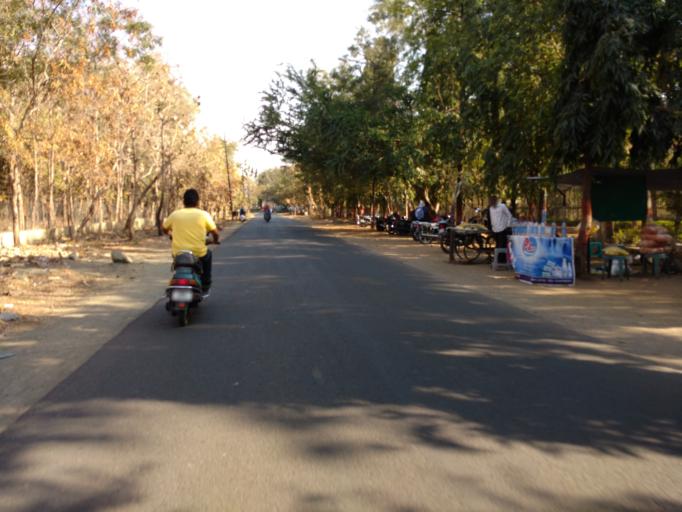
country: IN
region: Maharashtra
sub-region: Nagpur Division
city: Nagpur
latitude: 21.1687
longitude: 79.0598
